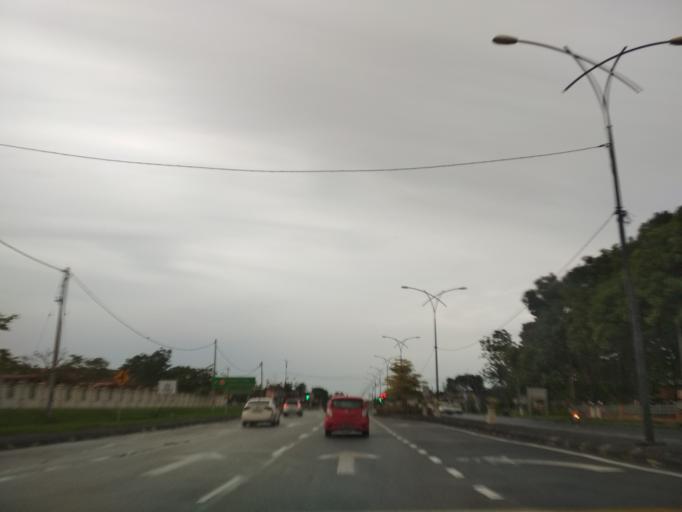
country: MY
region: Perlis
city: Kangar
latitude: 6.4527
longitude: 100.2065
